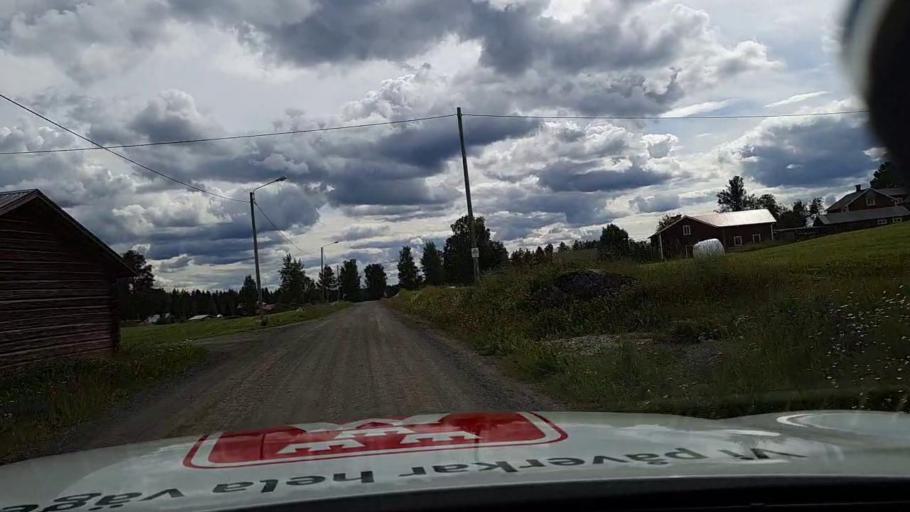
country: SE
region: Jaemtland
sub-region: Braecke Kommun
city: Braecke
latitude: 63.2835
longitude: 15.3706
